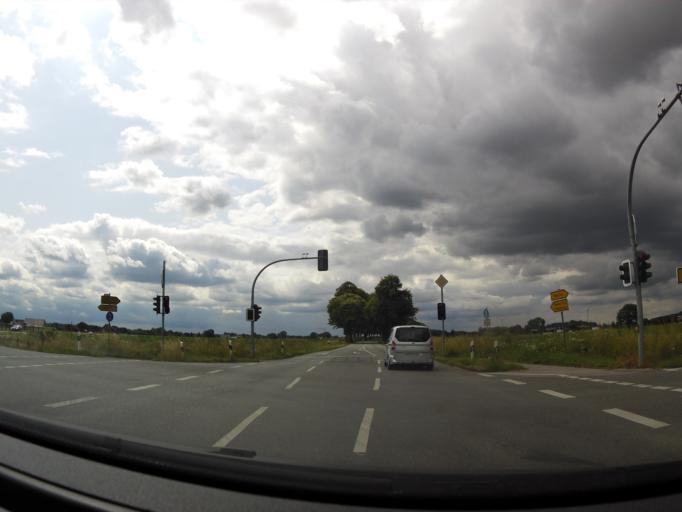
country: DE
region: North Rhine-Westphalia
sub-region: Regierungsbezirk Dusseldorf
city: Xanten
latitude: 51.6097
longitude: 6.4552
